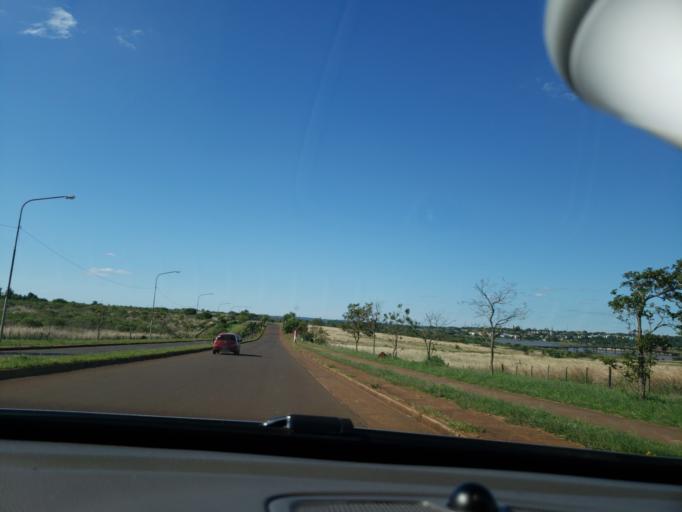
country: AR
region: Misiones
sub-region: Departamento de Capital
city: Posadas
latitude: -27.3898
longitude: -55.9619
